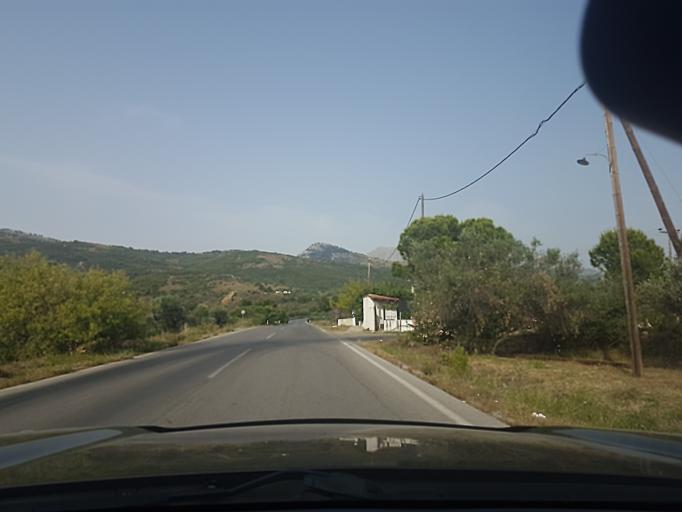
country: GR
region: Central Greece
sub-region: Nomos Evvoias
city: Yimnon
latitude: 38.5756
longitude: 23.8073
